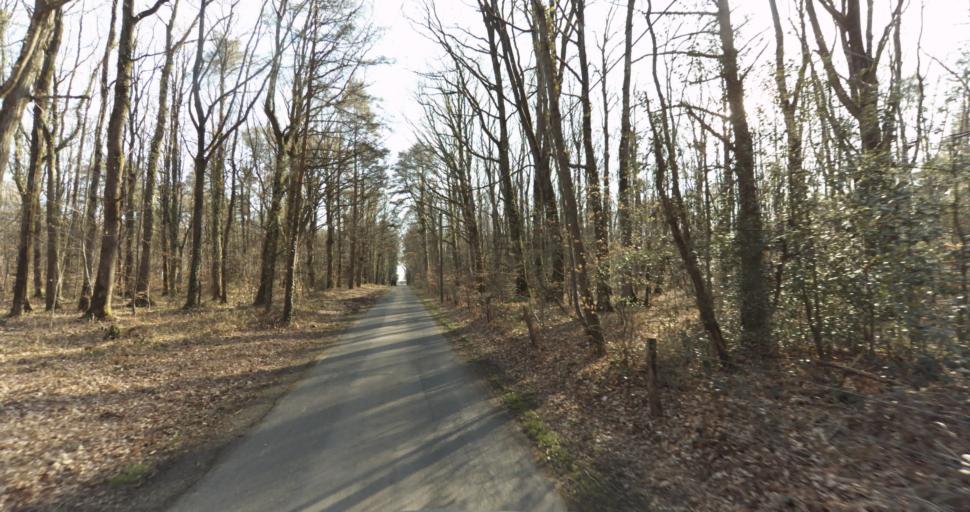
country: FR
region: Lower Normandy
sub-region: Departement du Calvados
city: Livarot
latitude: 48.9726
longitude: 0.0769
